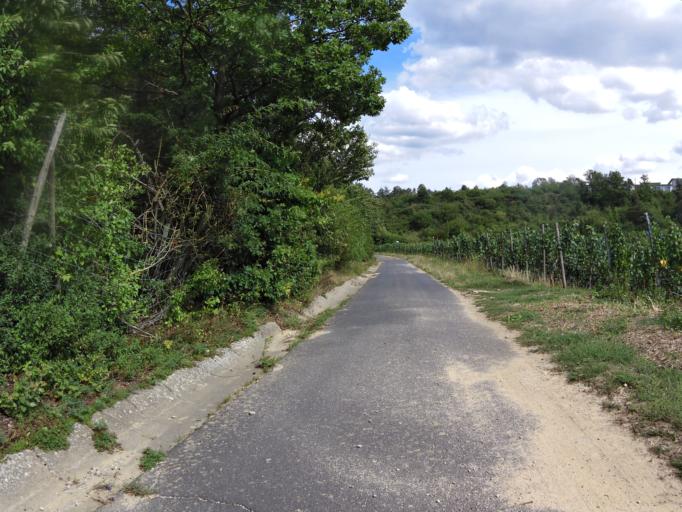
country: DE
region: Bavaria
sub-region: Regierungsbezirk Unterfranken
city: Sommerhausen
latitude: 49.7023
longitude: 10.0327
